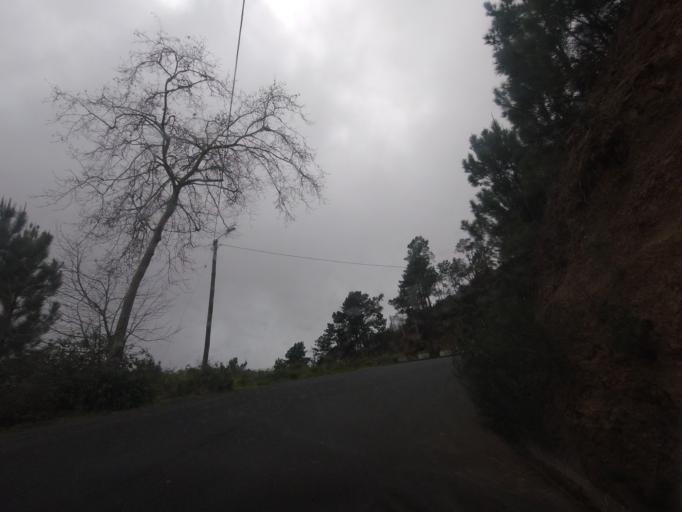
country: PT
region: Madeira
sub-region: Calheta
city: Faja da Ovelha
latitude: 32.7681
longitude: -17.2106
